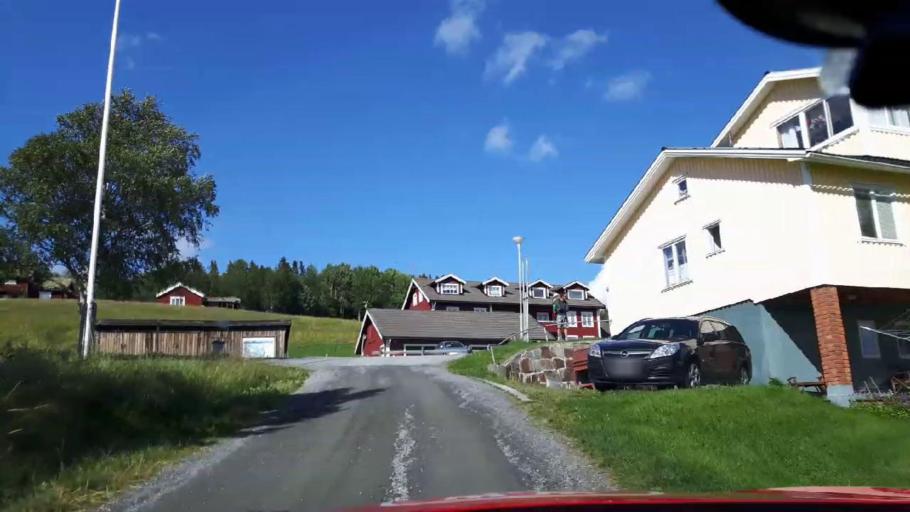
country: SE
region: Jaemtland
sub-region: Are Kommun
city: Are
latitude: 63.2153
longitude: 13.0555
